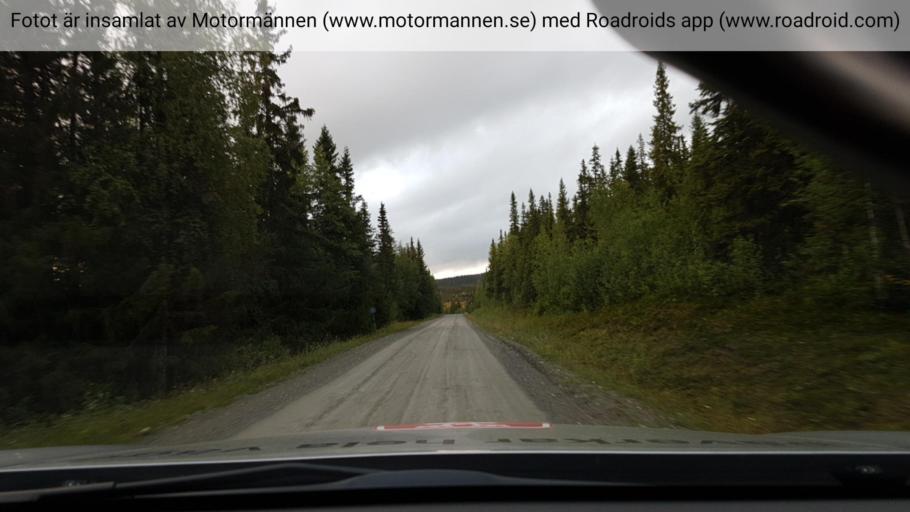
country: SE
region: Vaesterbotten
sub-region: Vilhelmina Kommun
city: Sjoberg
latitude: 65.5487
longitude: 15.4154
